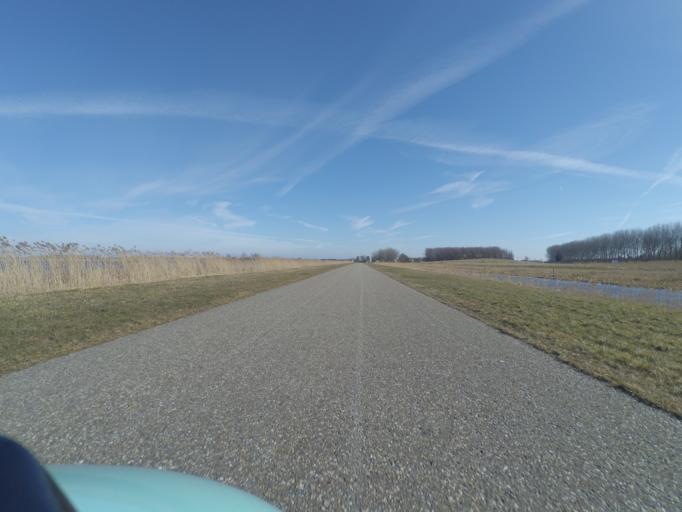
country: NL
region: Flevoland
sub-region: Gemeente Almere
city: Almere Stad
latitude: 52.3880
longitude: 5.1932
